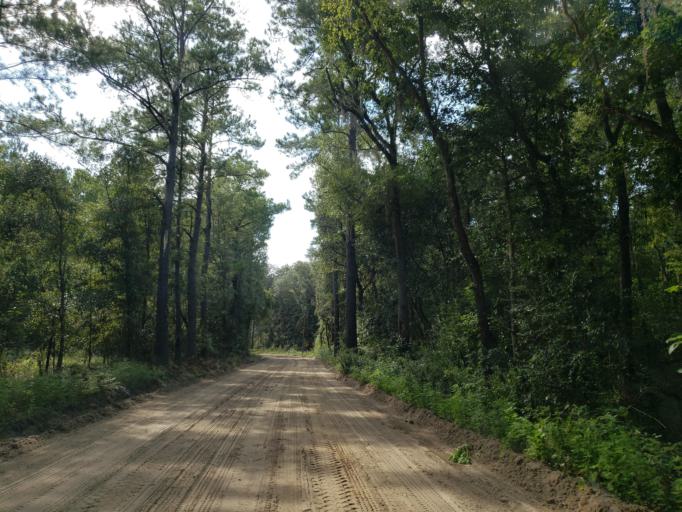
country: US
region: Georgia
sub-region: Echols County
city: Statenville
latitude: 30.6215
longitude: -83.2097
